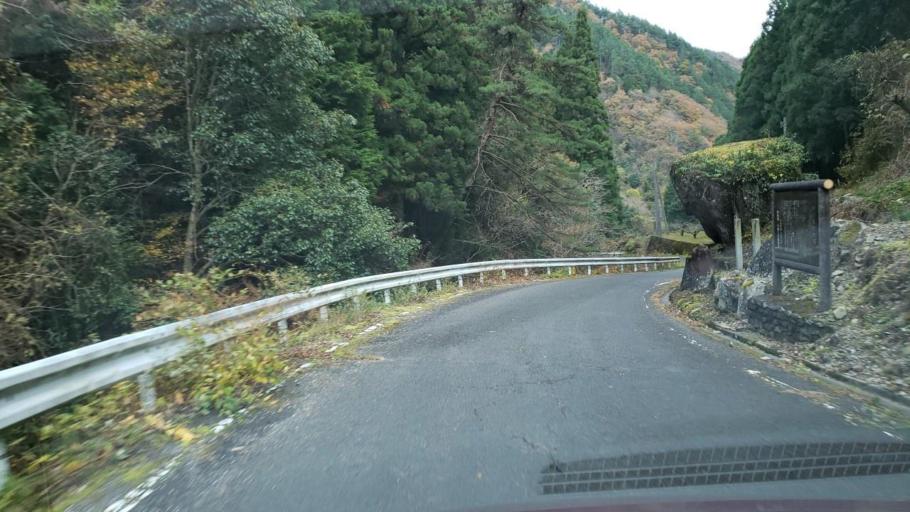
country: JP
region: Tokushima
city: Wakimachi
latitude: 34.1426
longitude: 134.2300
